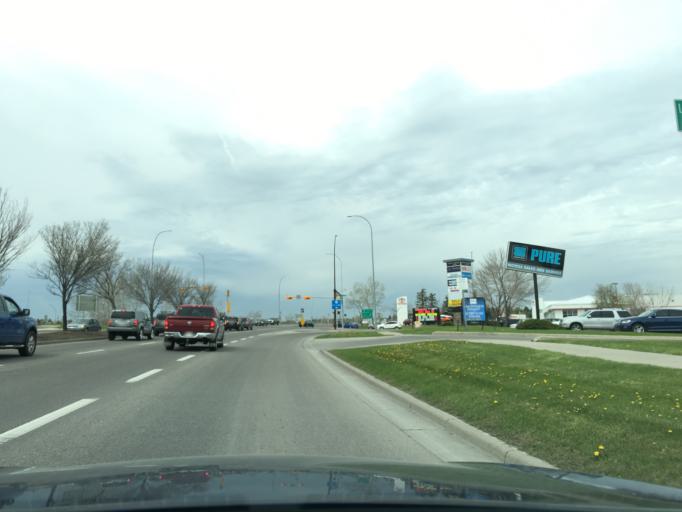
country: CA
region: Alberta
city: Calgary
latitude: 50.9302
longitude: -114.0644
